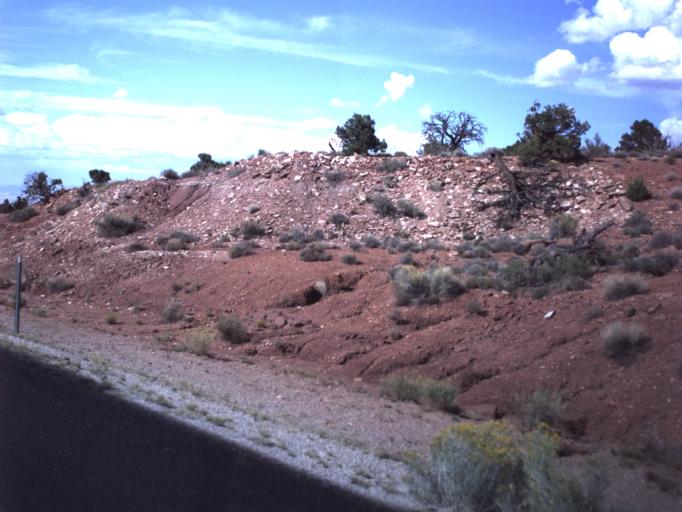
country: US
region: Utah
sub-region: Grand County
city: Moab
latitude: 38.5801
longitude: -109.7972
